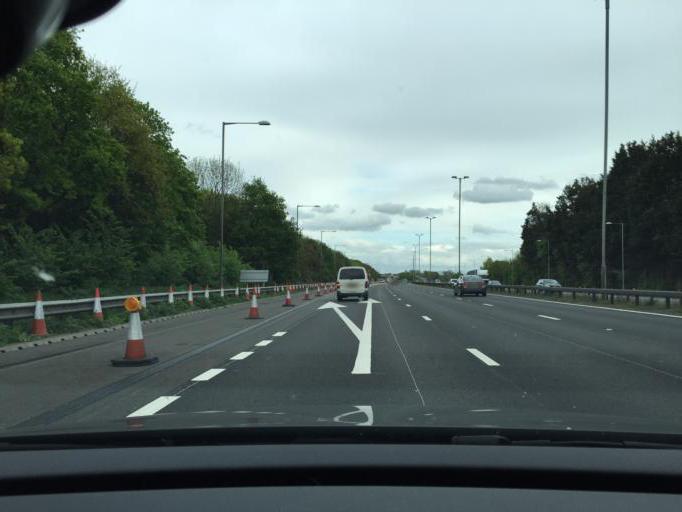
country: GB
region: England
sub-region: Wokingham
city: Shinfield
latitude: 51.4165
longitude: -0.9838
